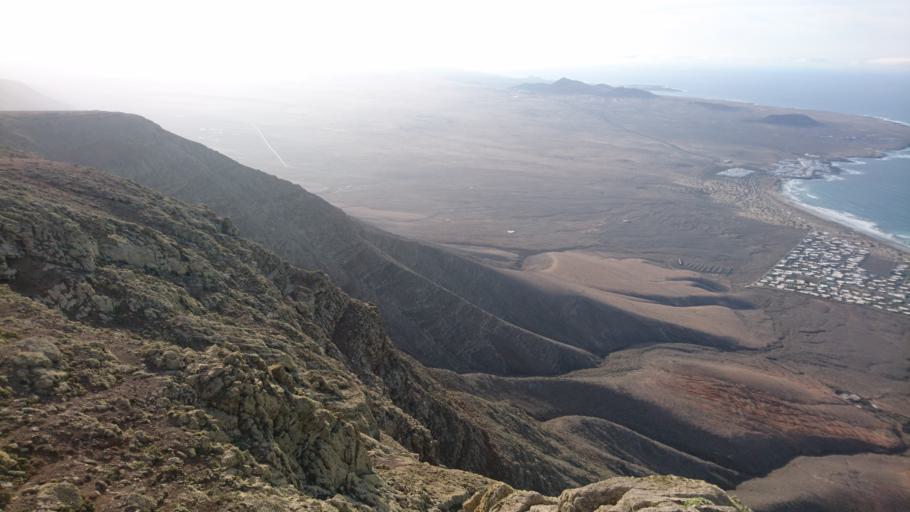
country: ES
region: Canary Islands
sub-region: Provincia de Las Palmas
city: Haria
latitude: 29.1070
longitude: -13.5307
